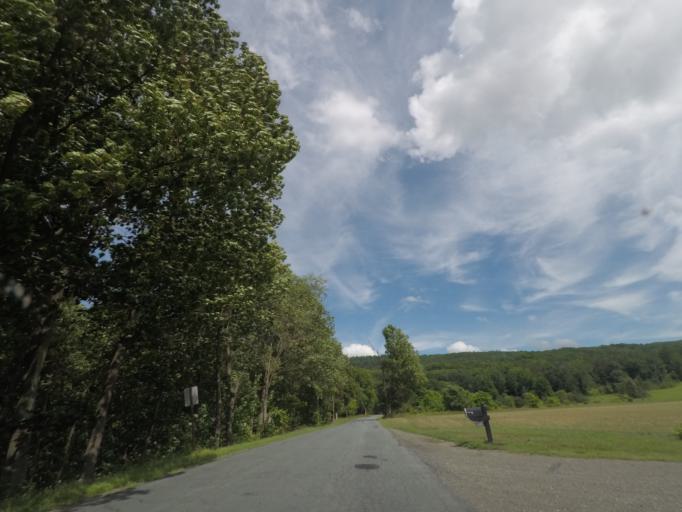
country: US
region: New York
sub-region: Rensselaer County
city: Poestenkill
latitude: 42.6862
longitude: -73.5587
